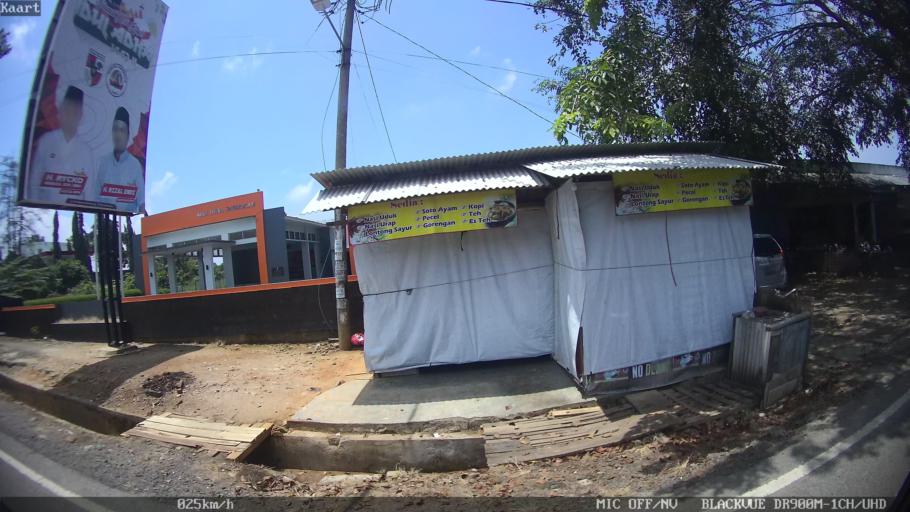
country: ID
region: Lampung
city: Kedaton
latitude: -5.3591
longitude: 105.2843
